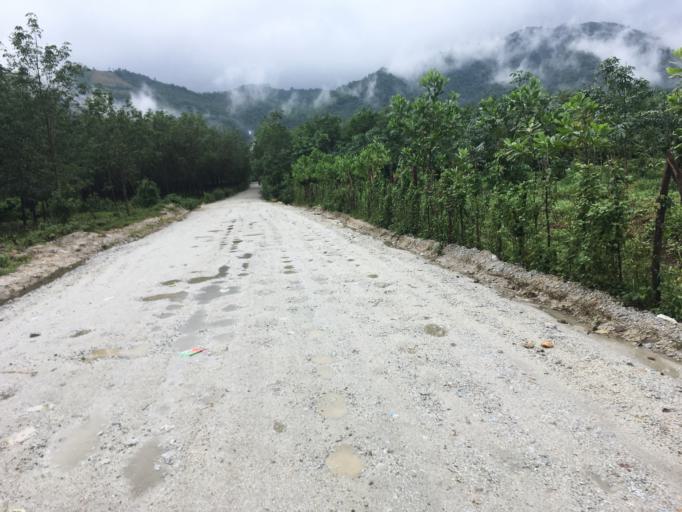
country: MM
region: Mon
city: Martaban
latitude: 16.6705
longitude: 97.5196
